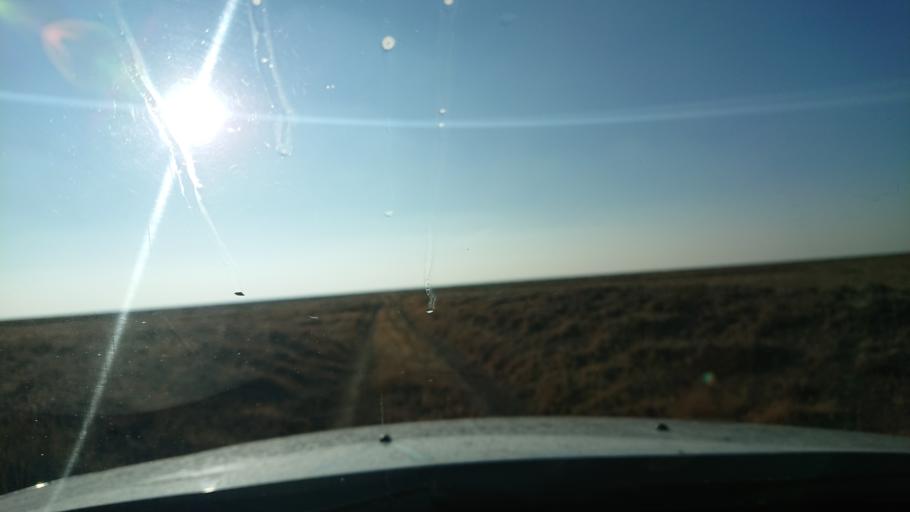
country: TR
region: Aksaray
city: Sultanhani
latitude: 38.3874
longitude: 33.5906
